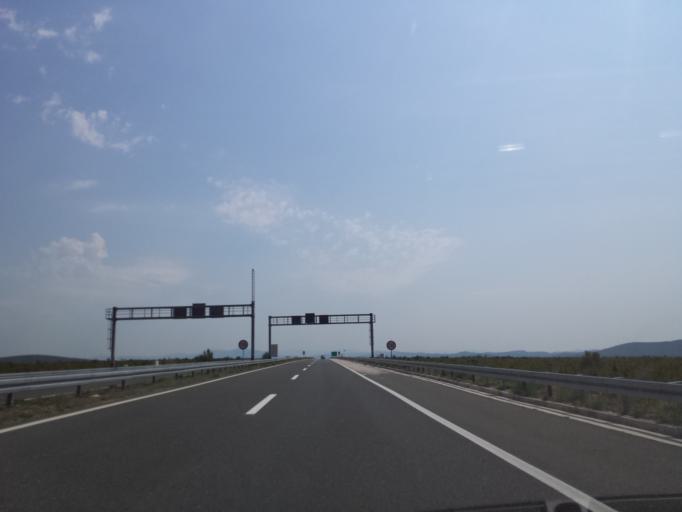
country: HR
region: Sibensko-Kniniska
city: Zaton
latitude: 43.8846
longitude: 15.7938
